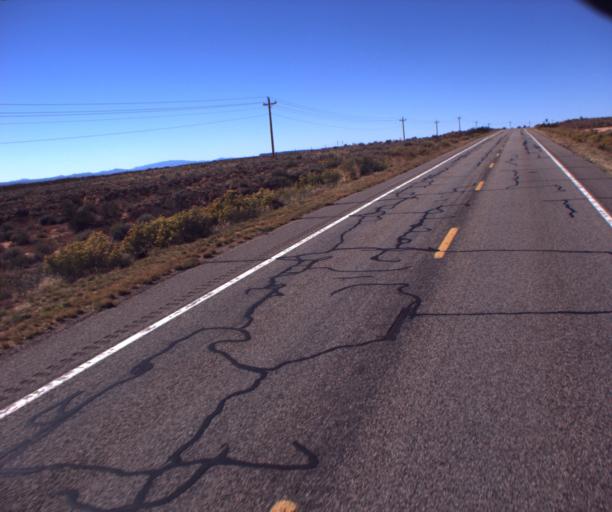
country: US
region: Arizona
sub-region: Coconino County
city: Fredonia
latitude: 36.8605
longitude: -112.7187
